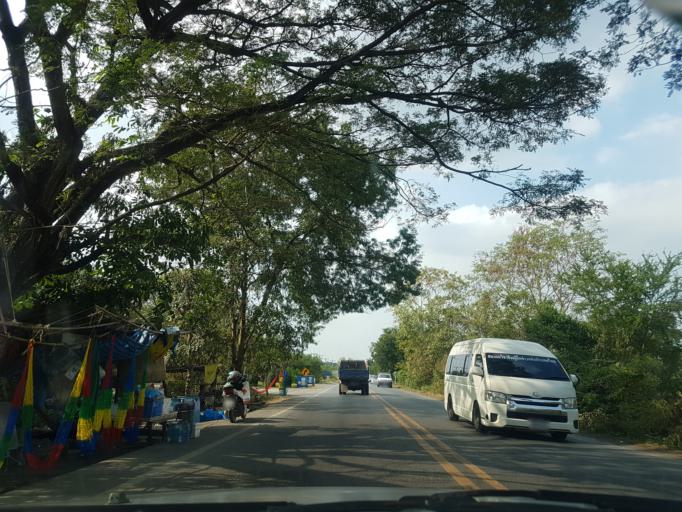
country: TH
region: Phra Nakhon Si Ayutthaya
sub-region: Amphoe Tha Ruea
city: Tha Ruea
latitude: 14.5549
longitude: 100.7231
